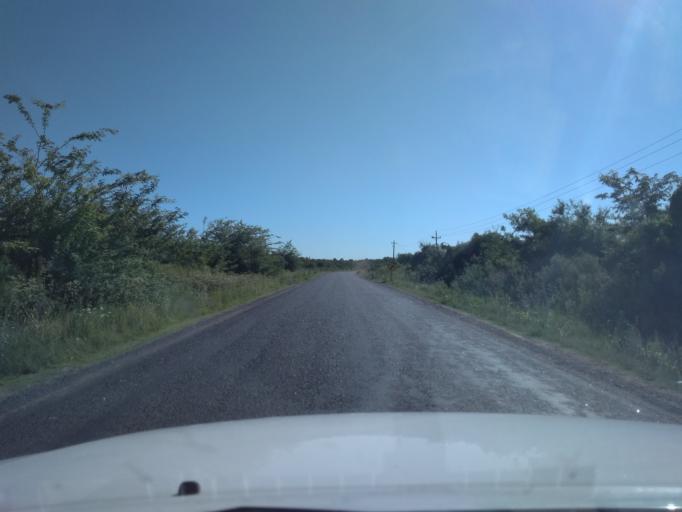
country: UY
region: Canelones
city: San Ramon
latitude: -34.2701
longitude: -55.9411
